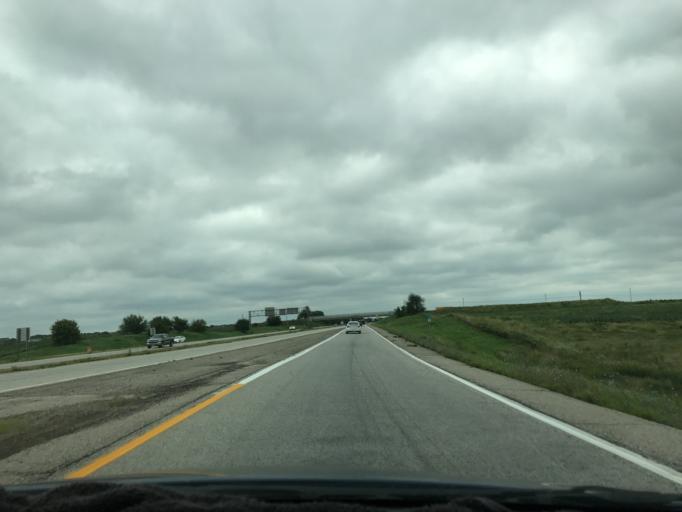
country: US
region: Iowa
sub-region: Scott County
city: Bettendorf
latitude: 41.5941
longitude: -90.5250
